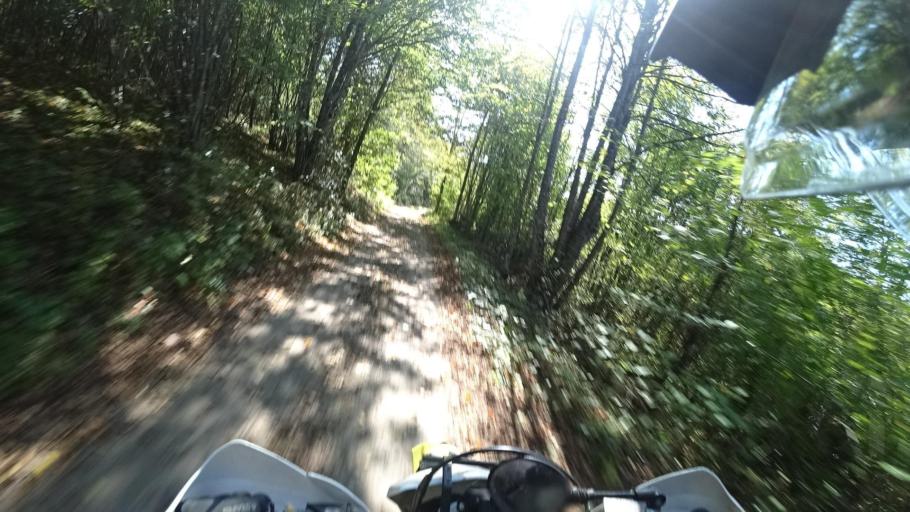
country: HR
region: Karlovacka
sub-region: Grad Ogulin
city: Ogulin
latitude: 45.2009
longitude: 15.1251
